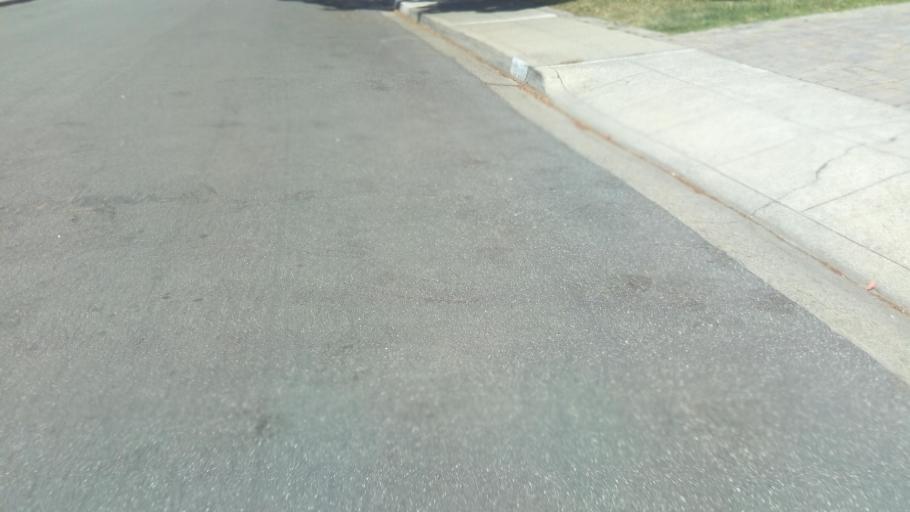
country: US
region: California
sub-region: Santa Clara County
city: Mountain View
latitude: 37.3704
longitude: -122.0942
